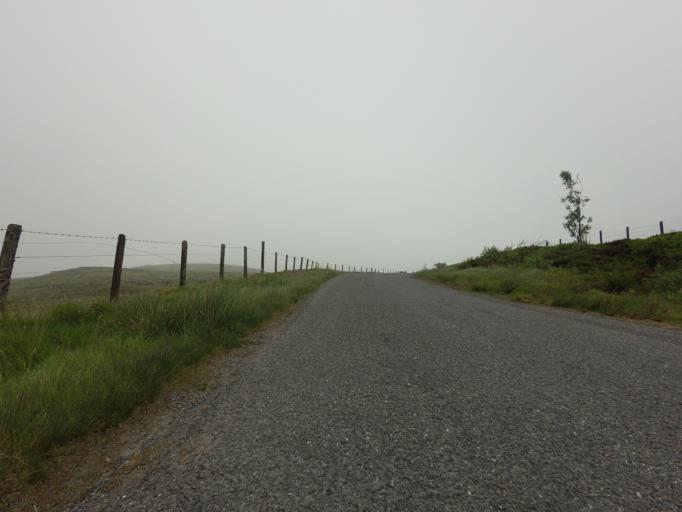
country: GB
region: Scotland
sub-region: Perth and Kinross
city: Kinross
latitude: 56.1543
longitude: -3.4533
